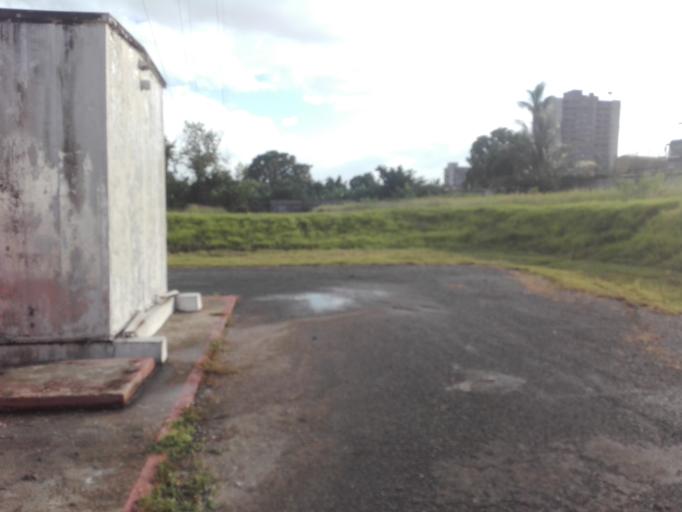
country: CU
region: Cienfuegos
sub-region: Municipio de Cienfuegos
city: Cienfuegos
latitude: 22.1714
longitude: -80.4460
